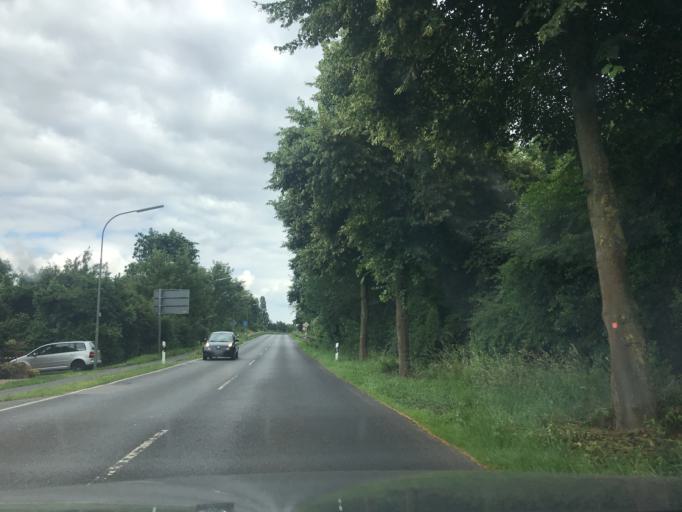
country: DE
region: North Rhine-Westphalia
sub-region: Regierungsbezirk Dusseldorf
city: Neubrueck
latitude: 51.1696
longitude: 6.6503
